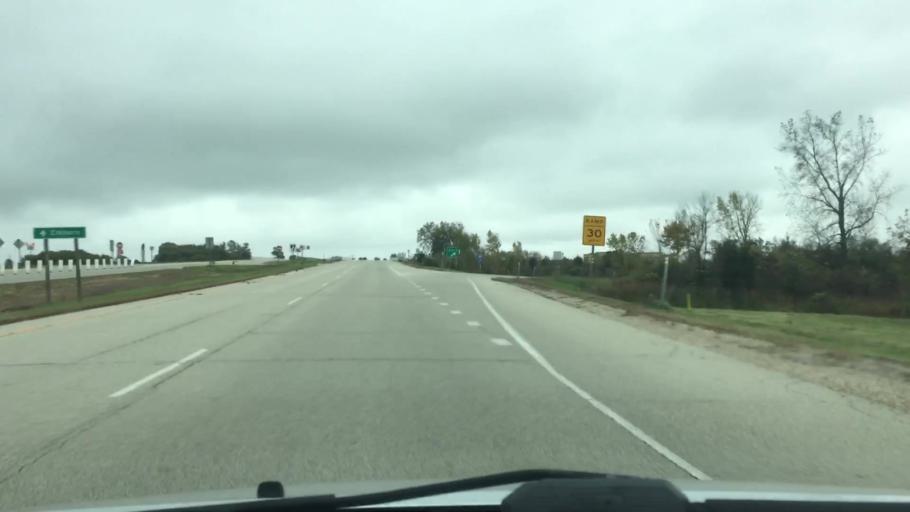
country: US
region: Wisconsin
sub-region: Walworth County
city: Elkhorn
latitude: 42.7001
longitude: -88.5420
